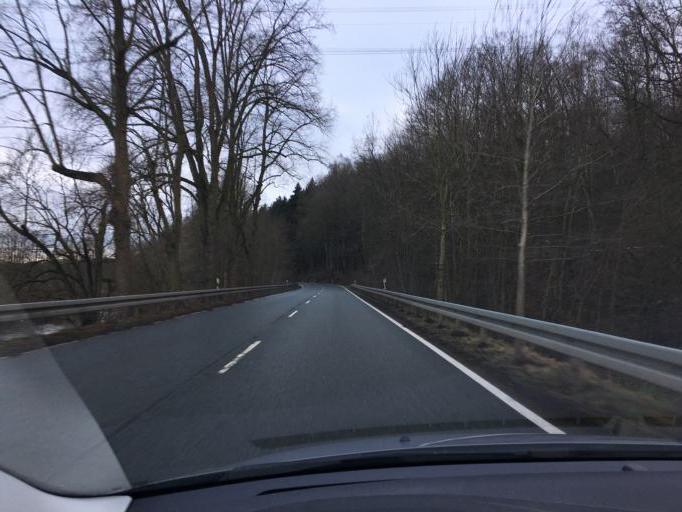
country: DE
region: Saxony
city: Waldenburg
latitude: 50.8923
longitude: 12.6266
